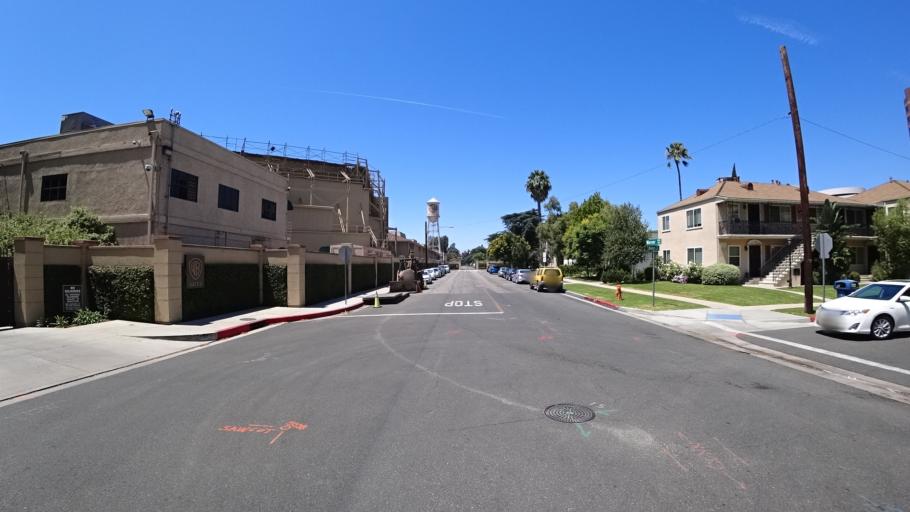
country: US
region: California
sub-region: Los Angeles County
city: Universal City
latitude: 34.1513
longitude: -118.3366
